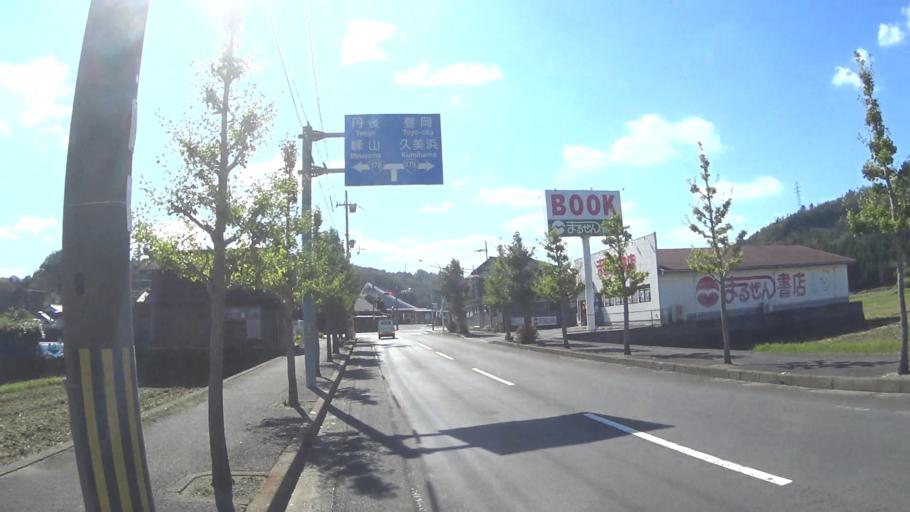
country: JP
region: Kyoto
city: Miyazu
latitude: 35.6684
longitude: 135.0250
